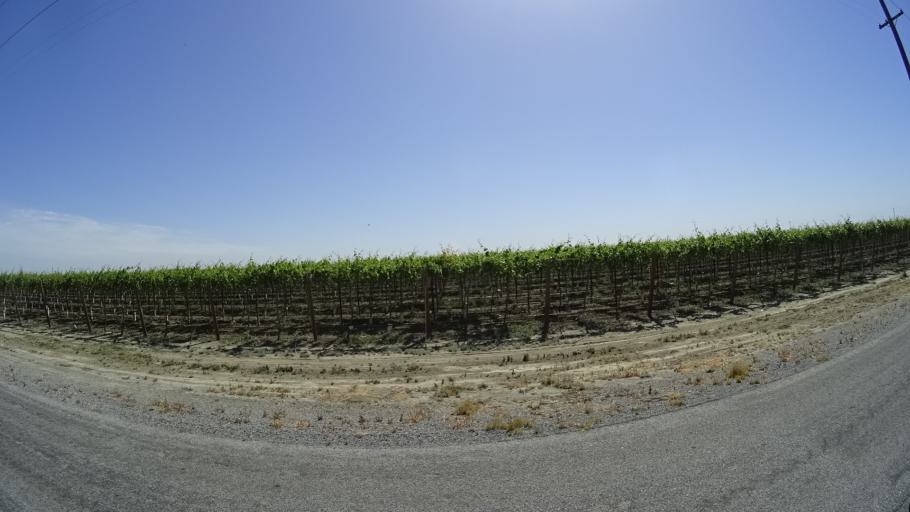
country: US
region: California
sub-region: Kings County
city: Stratford
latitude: 36.2353
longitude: -119.8343
